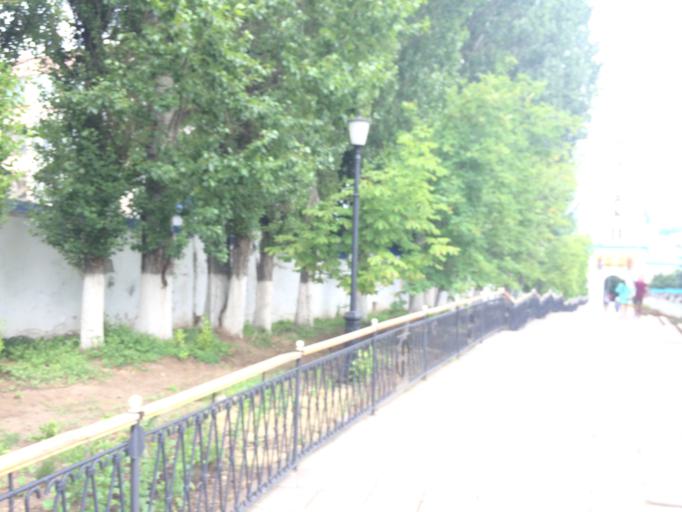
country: RU
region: Kursk
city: Zolotukhino
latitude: 51.9732
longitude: 36.3114
